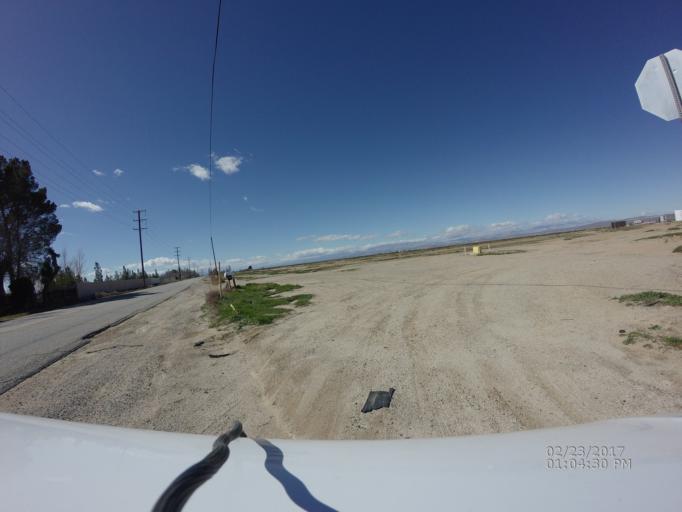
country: US
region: California
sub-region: Los Angeles County
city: Lancaster
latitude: 34.7634
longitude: -118.0146
